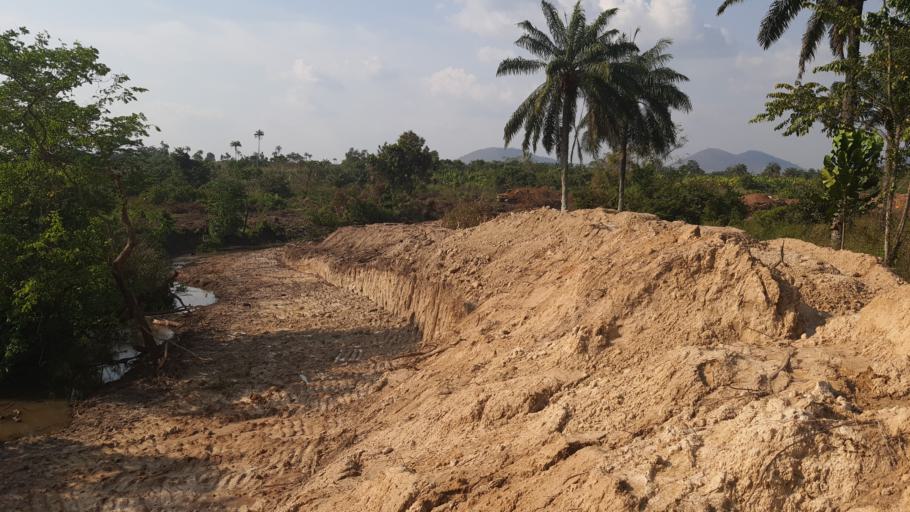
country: NG
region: Osun
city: Iwo
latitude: 7.7103
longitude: 4.1115
